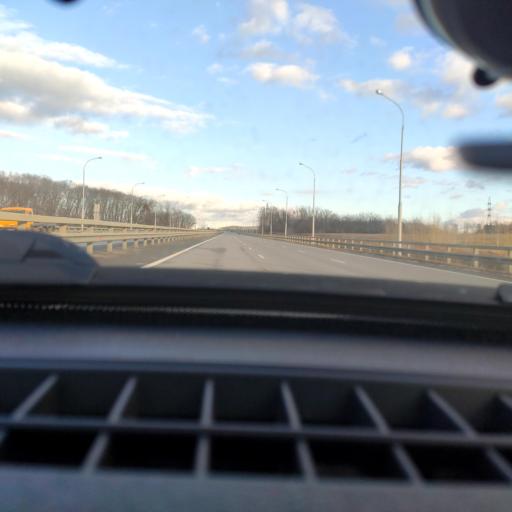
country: RU
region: Bashkortostan
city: Kabakovo
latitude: 54.6520
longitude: 56.0953
